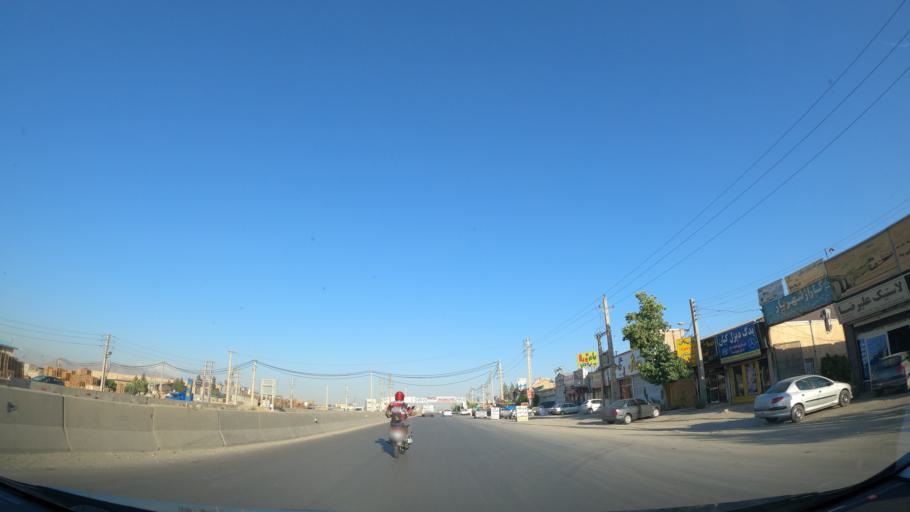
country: IR
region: Alborz
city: Hashtgerd
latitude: 35.9184
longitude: 50.7519
